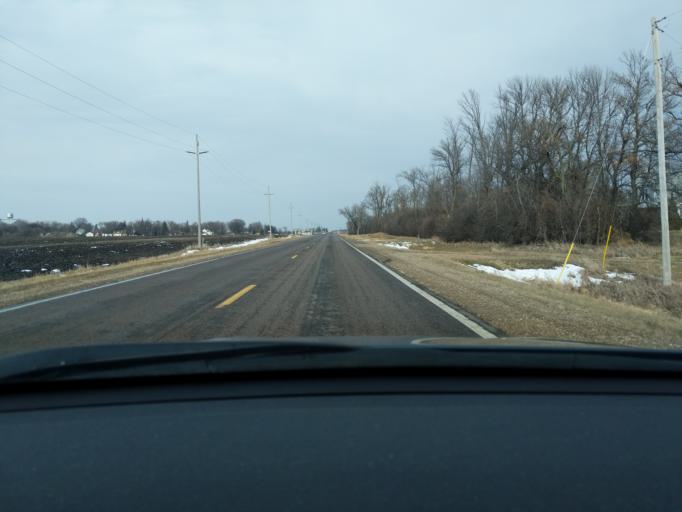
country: US
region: Minnesota
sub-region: Renville County
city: Renville
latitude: 44.7800
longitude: -95.3409
